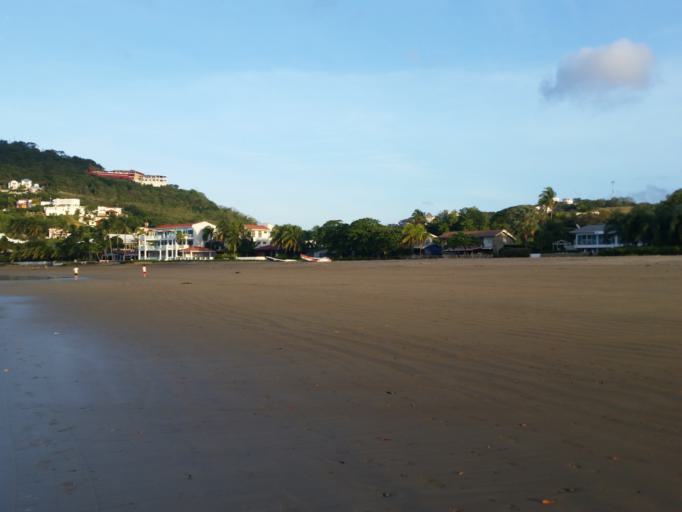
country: NI
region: Rivas
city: San Juan del Sur
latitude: 11.2593
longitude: -85.8755
